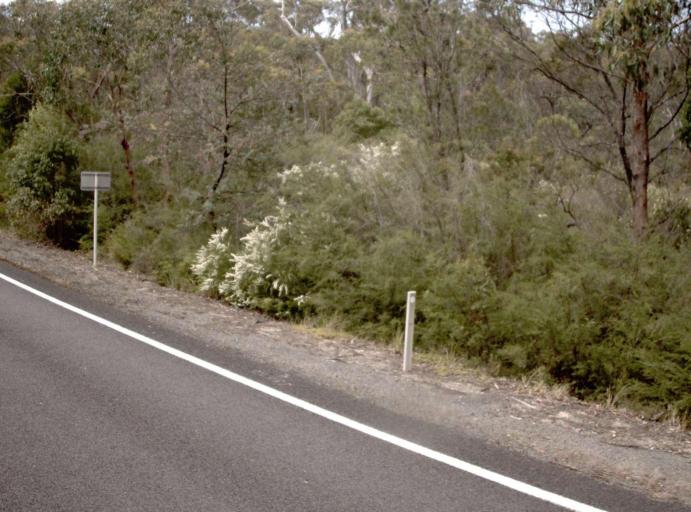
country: AU
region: New South Wales
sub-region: Bega Valley
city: Eden
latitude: -37.4871
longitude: 149.5502
